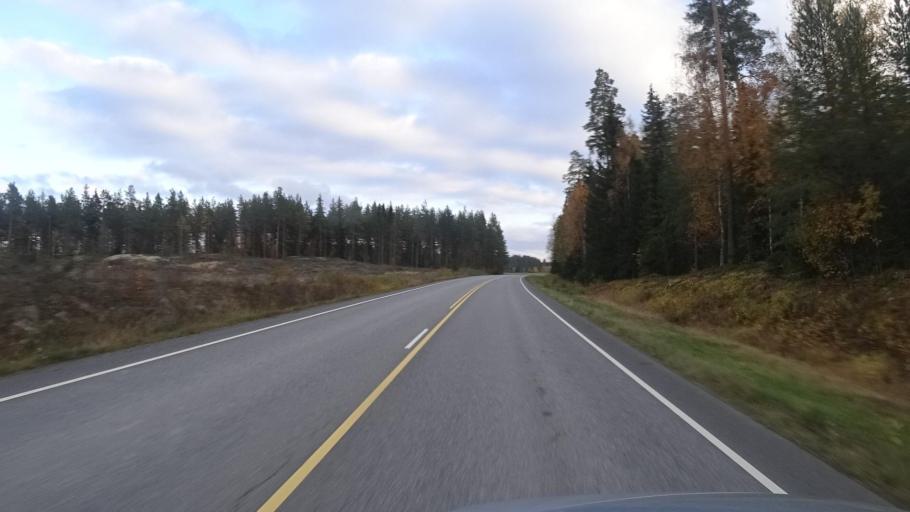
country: FI
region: Varsinais-Suomi
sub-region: Loimaa
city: Alastaro
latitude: 60.9277
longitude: 22.8854
